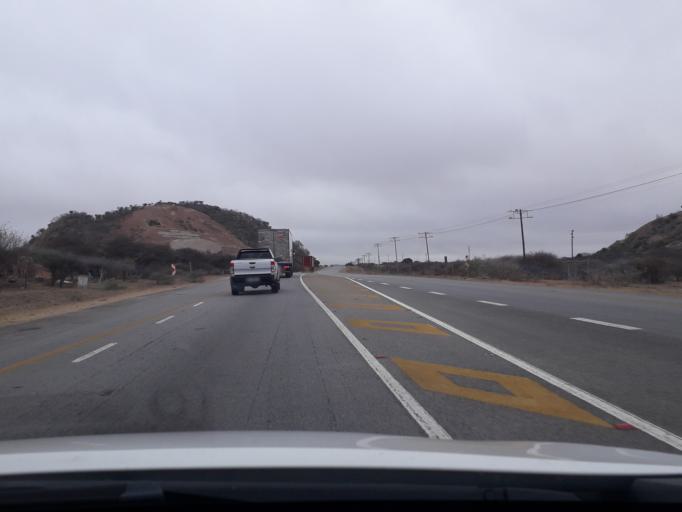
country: ZA
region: Limpopo
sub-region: Capricorn District Municipality
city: Mankoeng
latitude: -23.5294
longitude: 29.7041
